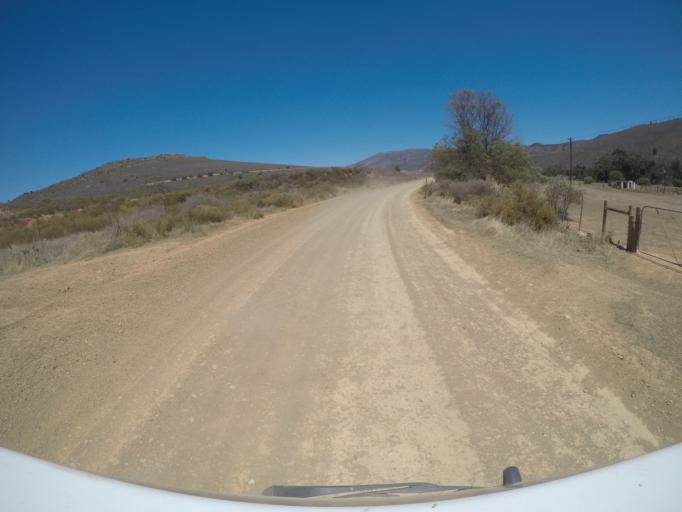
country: ZA
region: Western Cape
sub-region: Overberg District Municipality
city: Caledon
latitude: -34.1464
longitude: 19.2473
